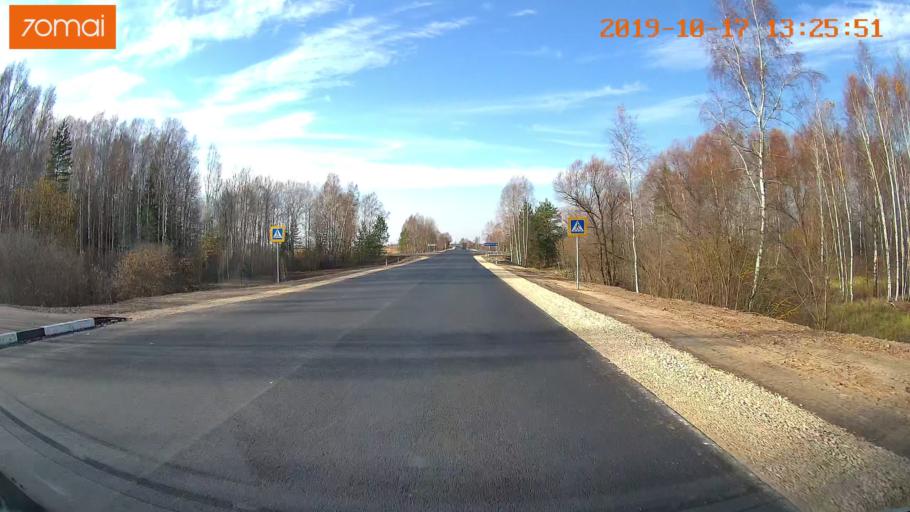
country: RU
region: Rjazan
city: Gus'-Zheleznyy
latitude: 55.1057
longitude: 40.9350
